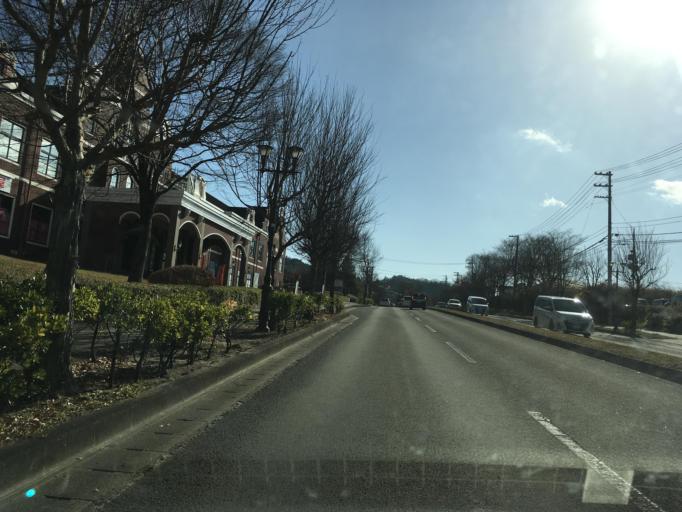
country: JP
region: Miyagi
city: Sendai
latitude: 38.2577
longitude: 140.7635
